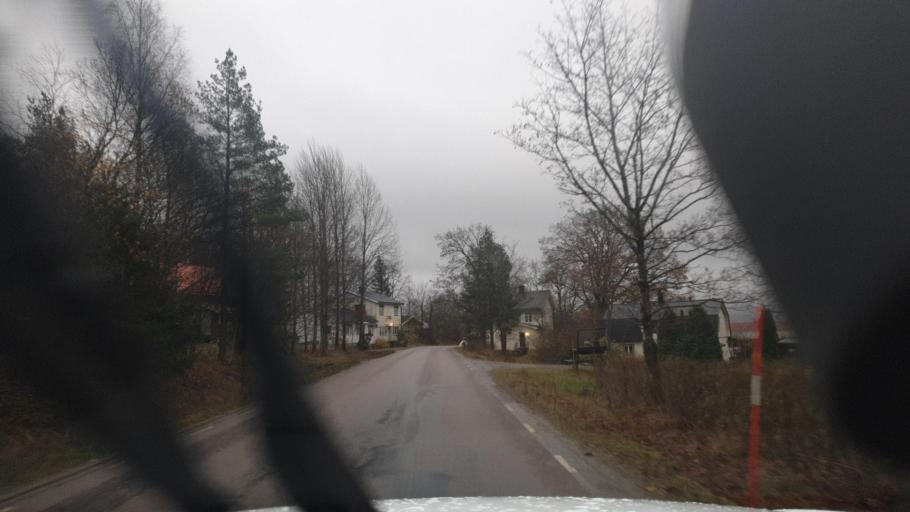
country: SE
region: Vaermland
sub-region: Eda Kommun
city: Charlottenberg
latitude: 59.7480
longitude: 12.1621
